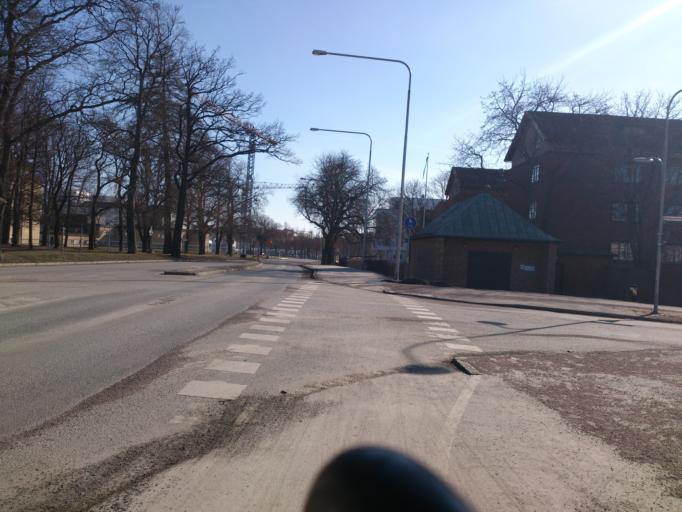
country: SE
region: Uppsala
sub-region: Uppsala Kommun
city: Uppsala
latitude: 59.8502
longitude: 17.6351
